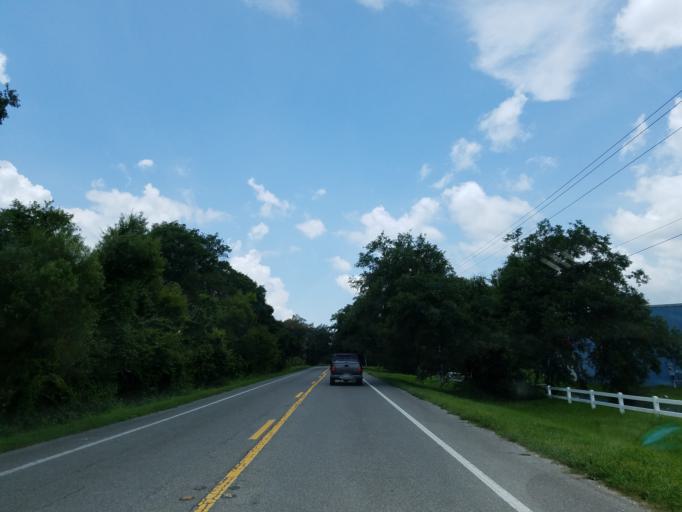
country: US
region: Florida
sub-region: Hillsborough County
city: Fish Hawk
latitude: 27.8506
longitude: -82.1227
